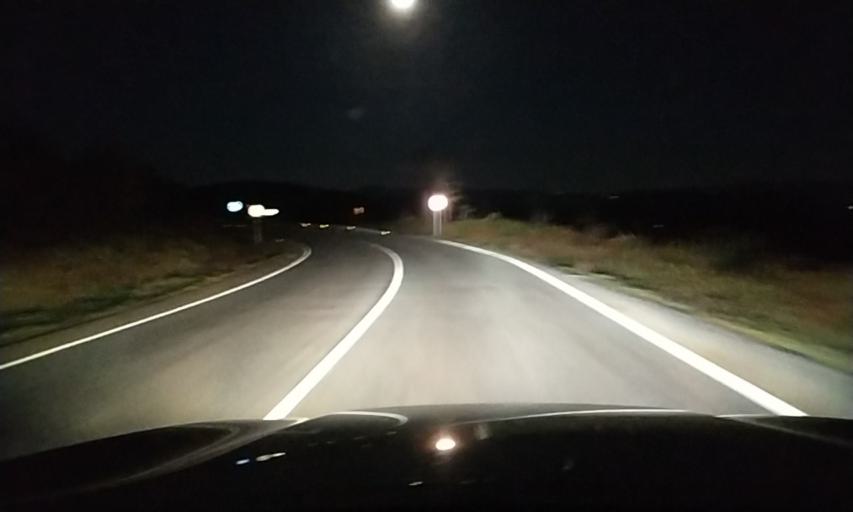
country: ES
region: Galicia
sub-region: Provincia de Ourense
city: Cualedro
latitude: 41.9804
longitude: -7.5269
